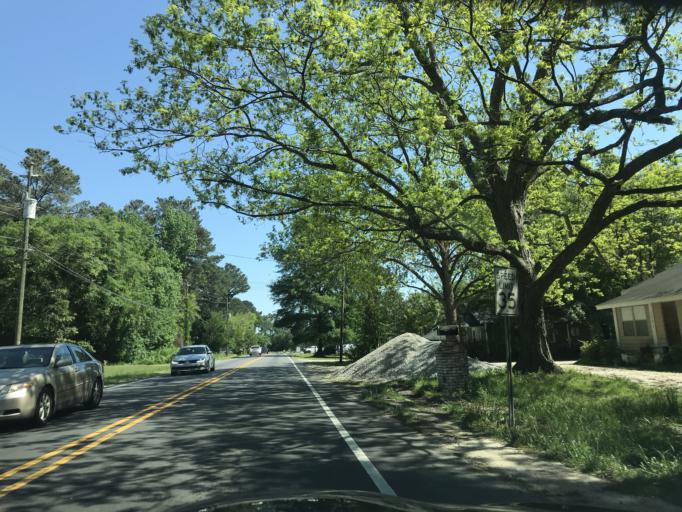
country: US
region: North Carolina
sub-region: Wake County
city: Garner
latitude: 35.7161
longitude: -78.6235
